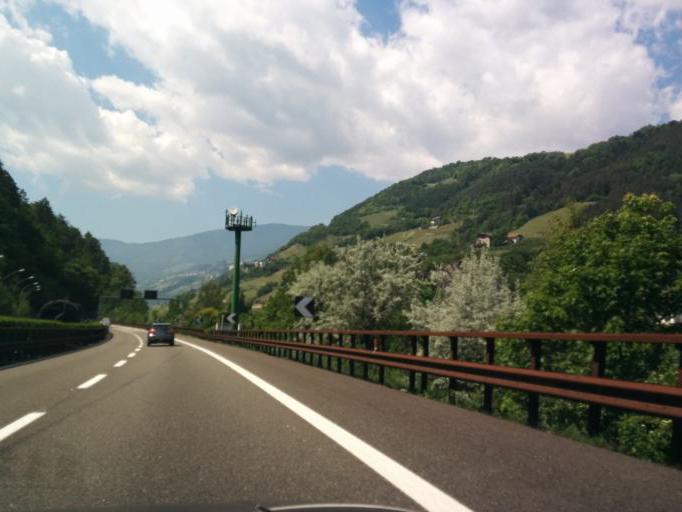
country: IT
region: Trentino-Alto Adige
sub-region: Bolzano
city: Velturno
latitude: 46.6532
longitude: 11.5937
